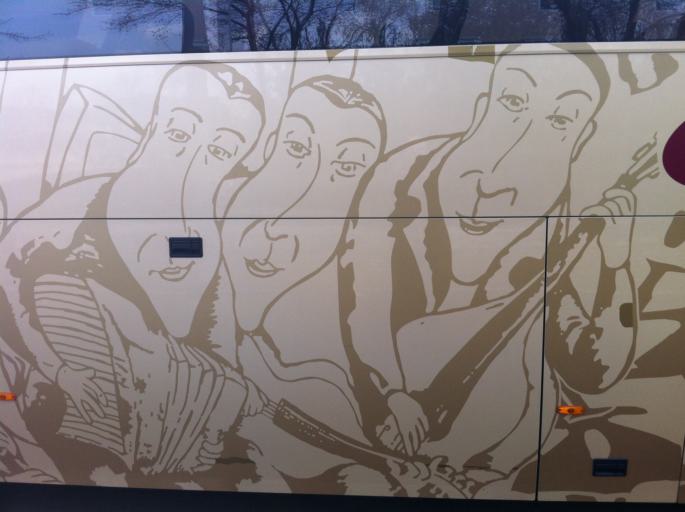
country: VA
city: Vatican City
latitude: 41.9183
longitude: 12.4717
